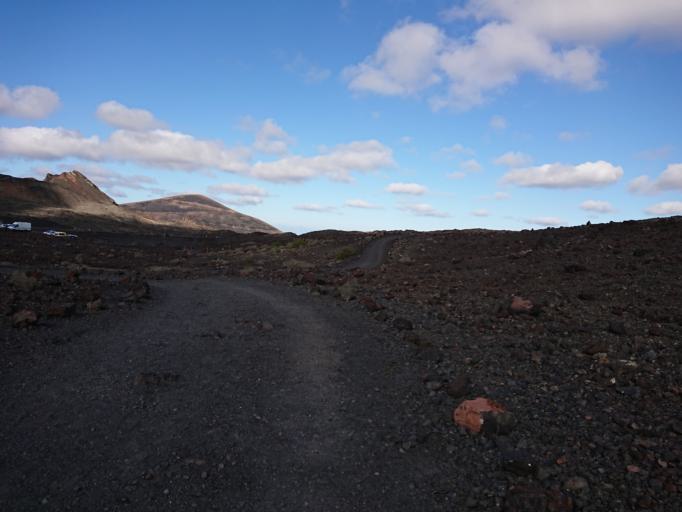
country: ES
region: Canary Islands
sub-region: Provincia de Las Palmas
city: Tias
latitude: 29.0041
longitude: -13.6823
